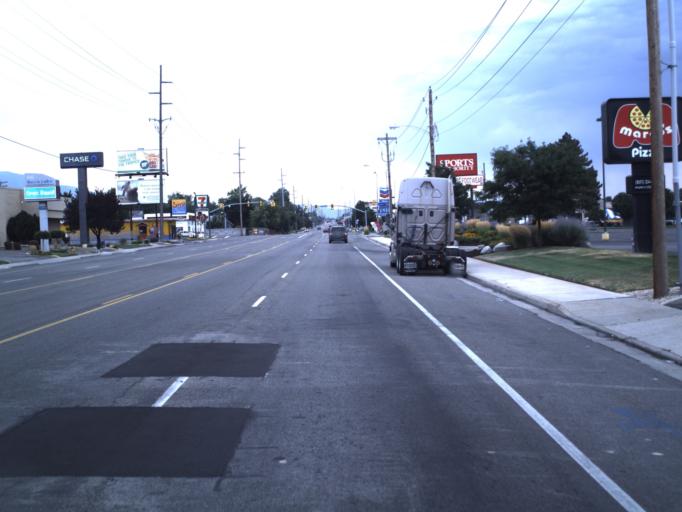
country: US
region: Utah
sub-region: Salt Lake County
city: Murray
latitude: 40.6513
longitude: -111.8660
